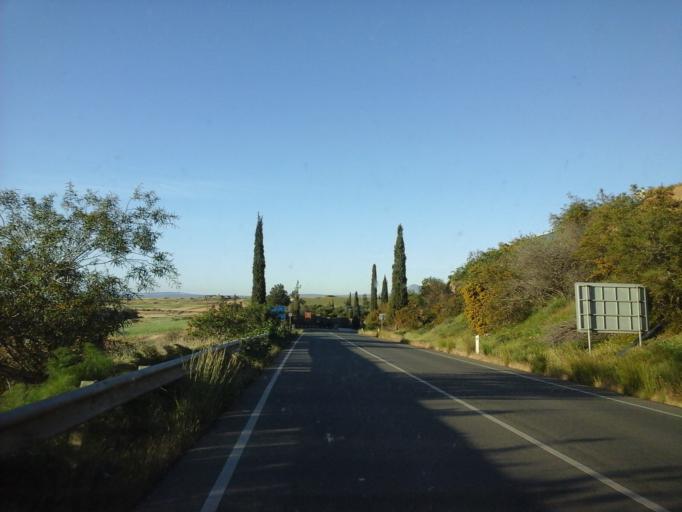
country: CY
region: Lefkosia
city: Astromeritis
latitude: 35.1028
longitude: 32.9716
